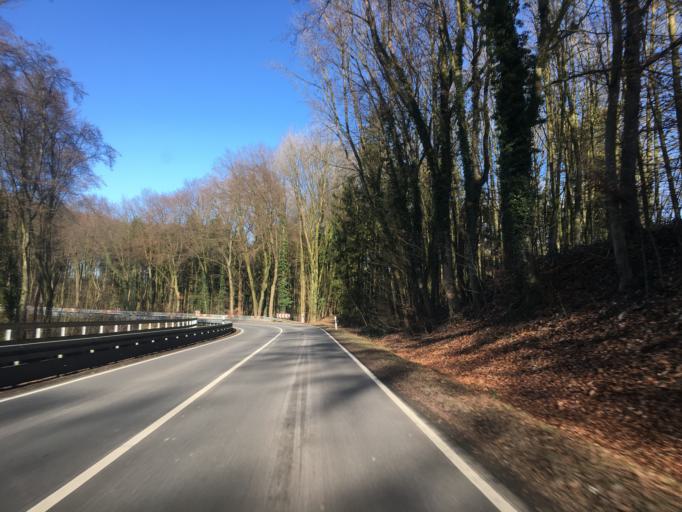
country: DE
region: North Rhine-Westphalia
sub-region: Regierungsbezirk Munster
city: Billerbeck
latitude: 51.9926
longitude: 7.2909
